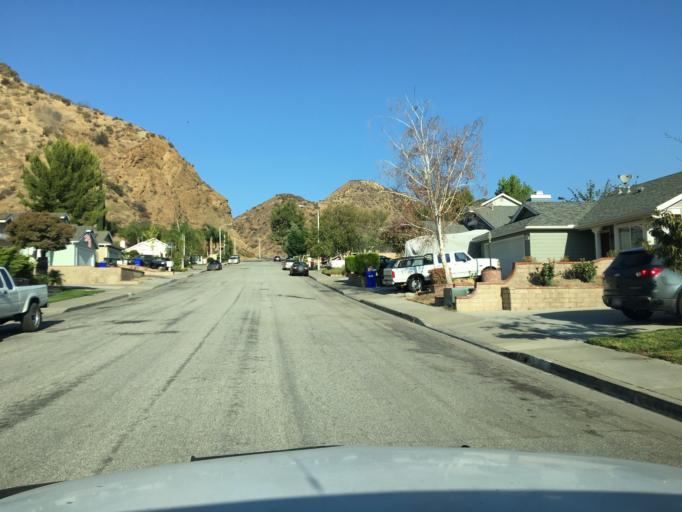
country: US
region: California
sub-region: Los Angeles County
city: Castaic
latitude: 34.5068
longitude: -118.6366
